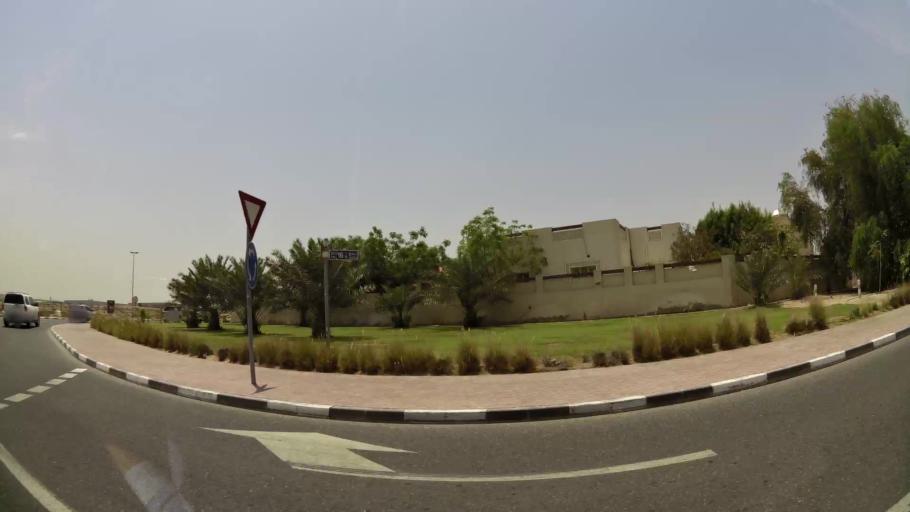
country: AE
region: Ash Shariqah
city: Sharjah
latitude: 25.1908
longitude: 55.3791
